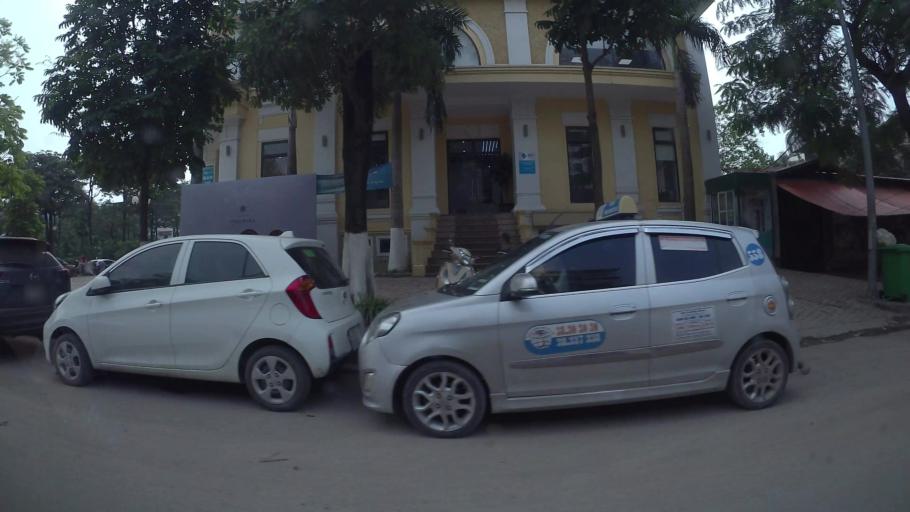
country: VN
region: Ha Noi
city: Van Dien
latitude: 20.9761
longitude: 105.8359
